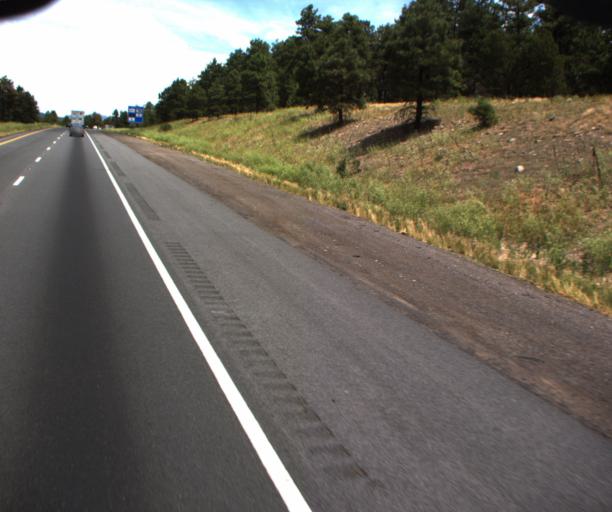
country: US
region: Arizona
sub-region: Coconino County
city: Williams
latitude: 35.2279
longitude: -112.2353
